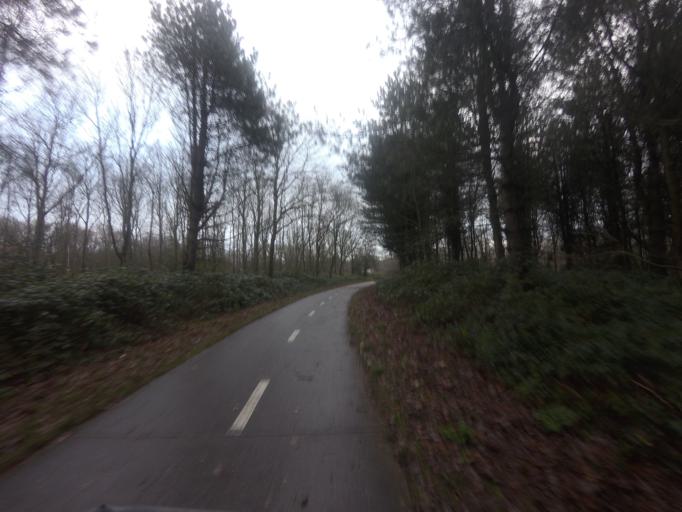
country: NL
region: North Holland
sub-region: Gemeente Texel
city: Den Burg
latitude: 53.1522
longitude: 4.8642
